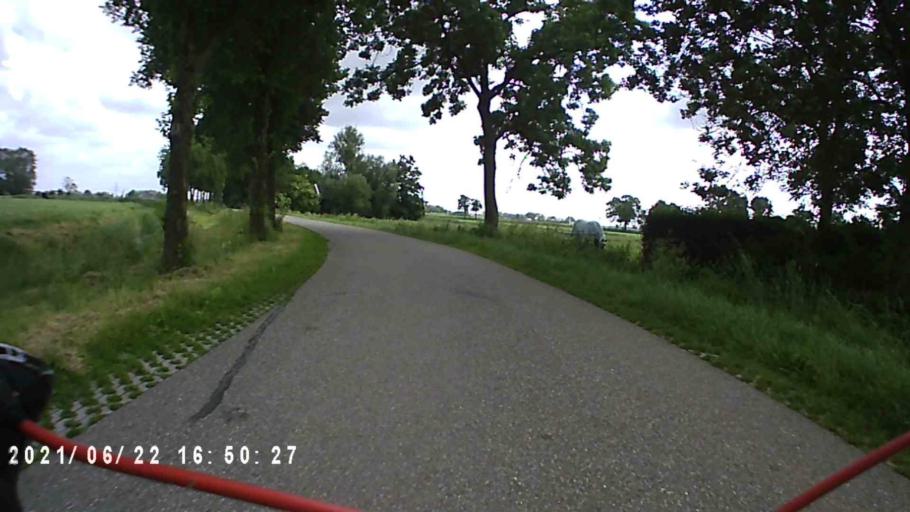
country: NL
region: Groningen
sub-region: Gemeente Bedum
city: Bedum
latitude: 53.3317
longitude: 6.6367
